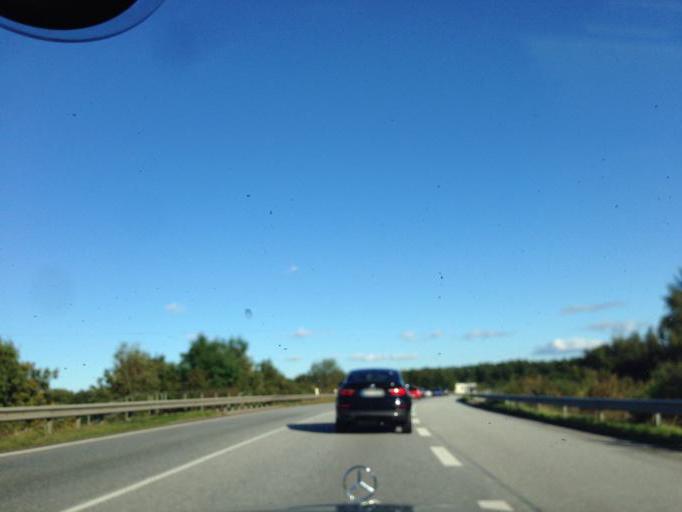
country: DE
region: Schleswig-Holstein
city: Boostedt
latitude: 54.0396
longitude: 10.0222
